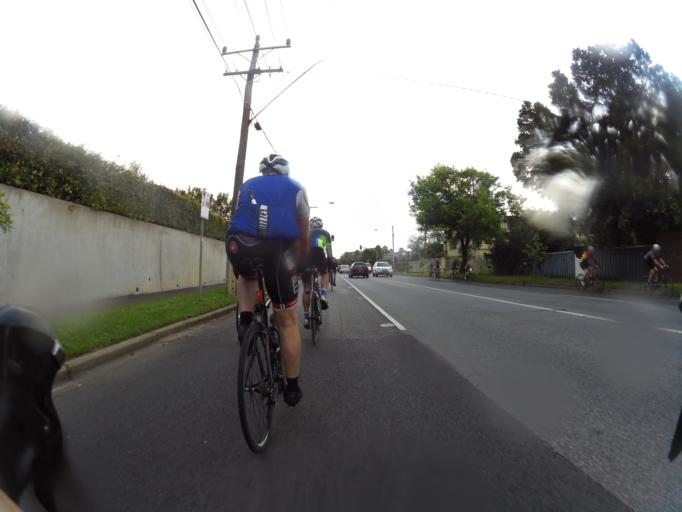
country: AU
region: Victoria
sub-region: Port Phillip
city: Elwood
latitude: -37.8950
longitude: 144.9901
